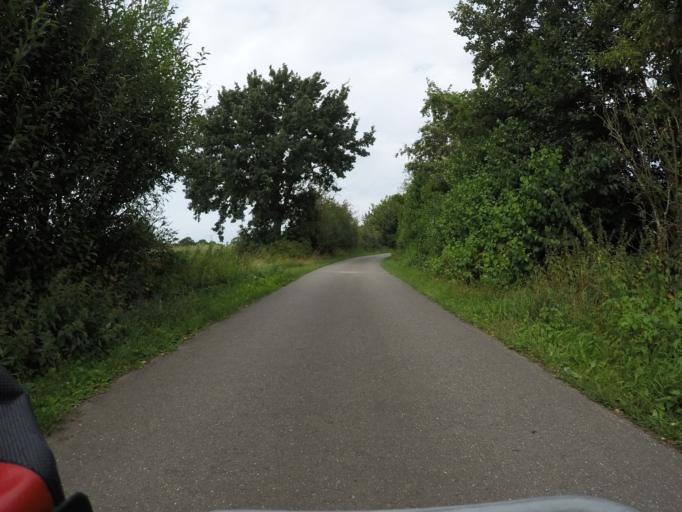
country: DE
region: Lower Saxony
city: Winsen
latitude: 53.3848
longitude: 10.2233
